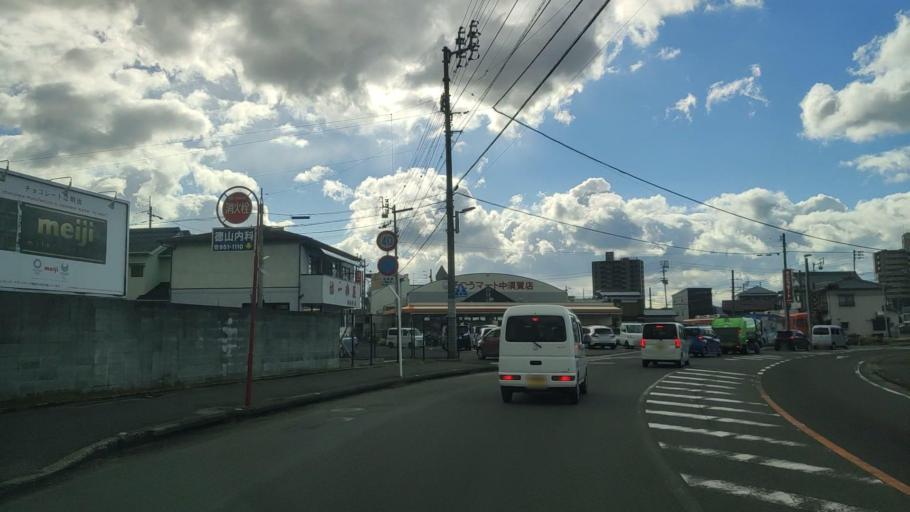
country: JP
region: Ehime
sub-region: Shikoku-chuo Shi
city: Matsuyama
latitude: 33.8659
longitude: 132.7193
